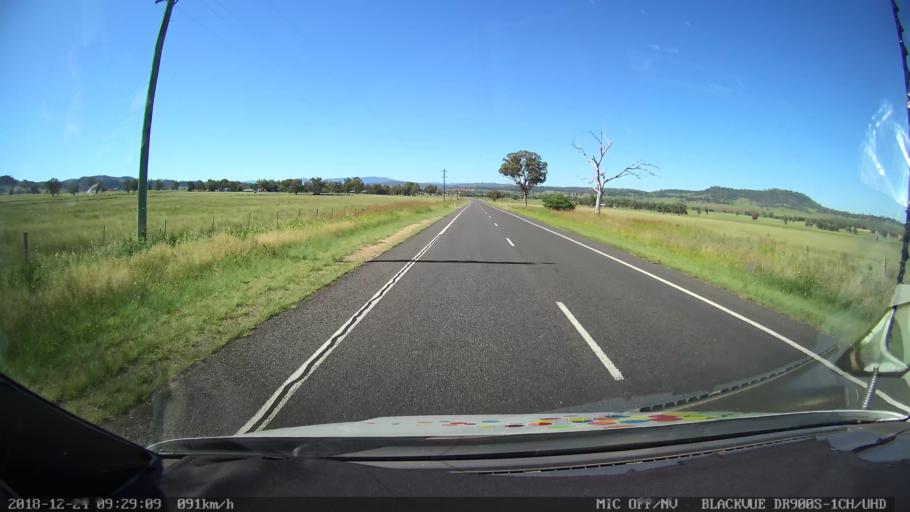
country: AU
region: New South Wales
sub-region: Liverpool Plains
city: Quirindi
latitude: -31.5467
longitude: 150.6925
